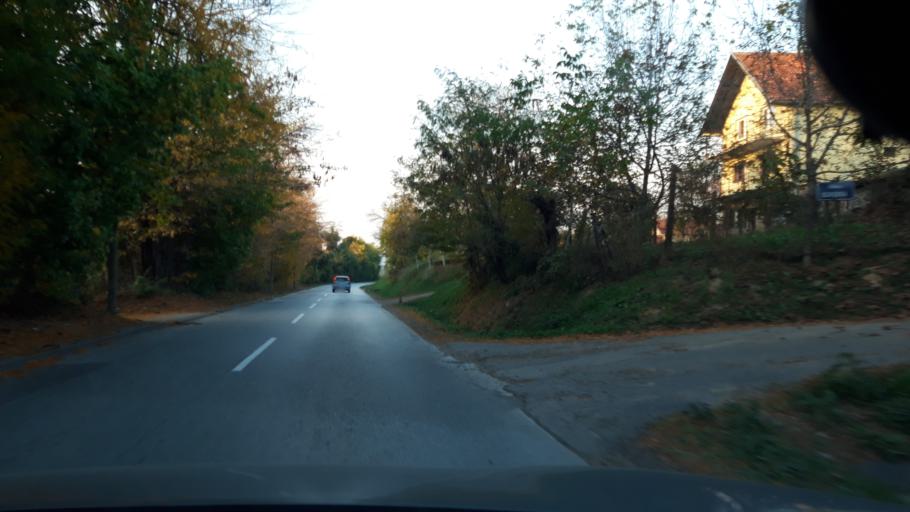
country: RS
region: Autonomna Pokrajina Vojvodina
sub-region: Juznobacki Okrug
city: Novi Sad
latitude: 45.2067
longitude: 19.8410
